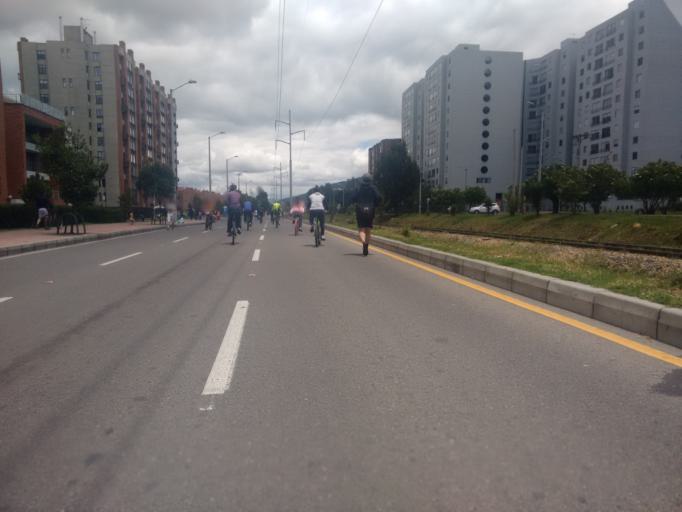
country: CO
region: Cundinamarca
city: La Calera
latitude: 4.7438
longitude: -74.0319
